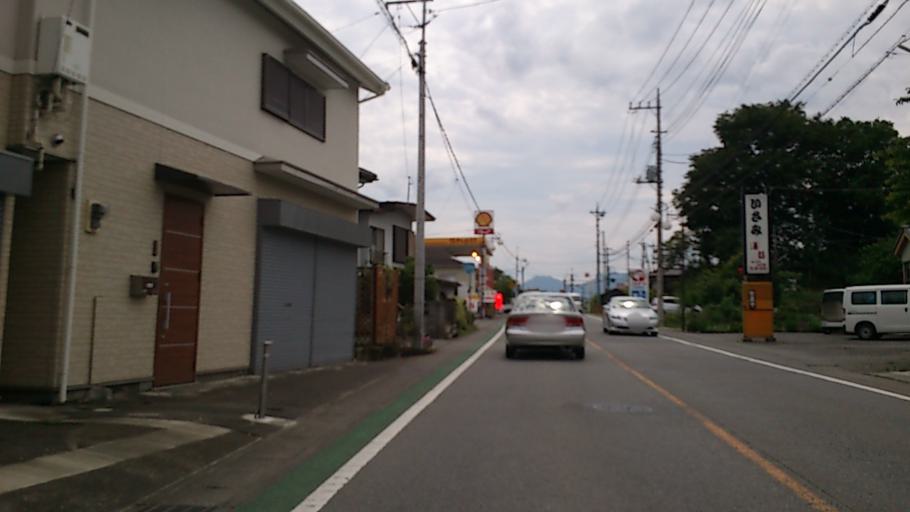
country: JP
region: Gunma
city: Tomioka
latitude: 36.2565
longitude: 138.8729
